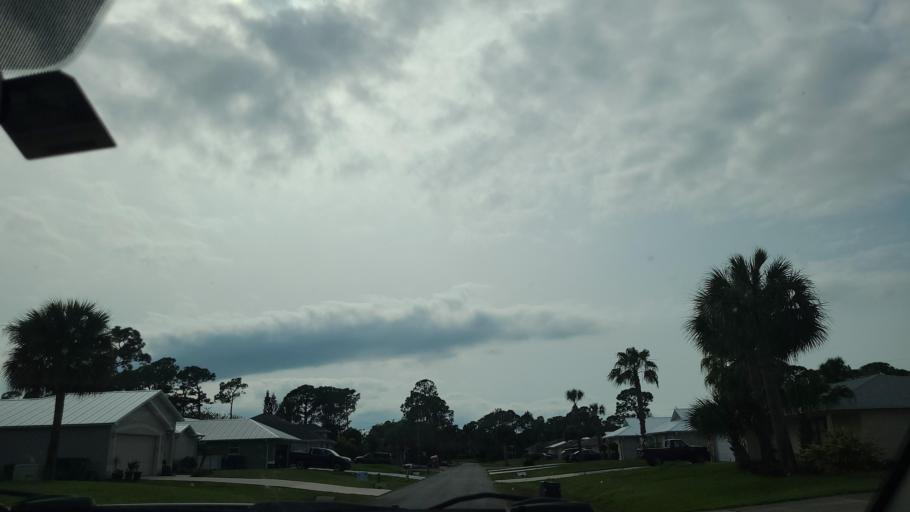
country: US
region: Florida
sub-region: Indian River County
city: Sebastian
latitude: 27.7866
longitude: -80.4824
